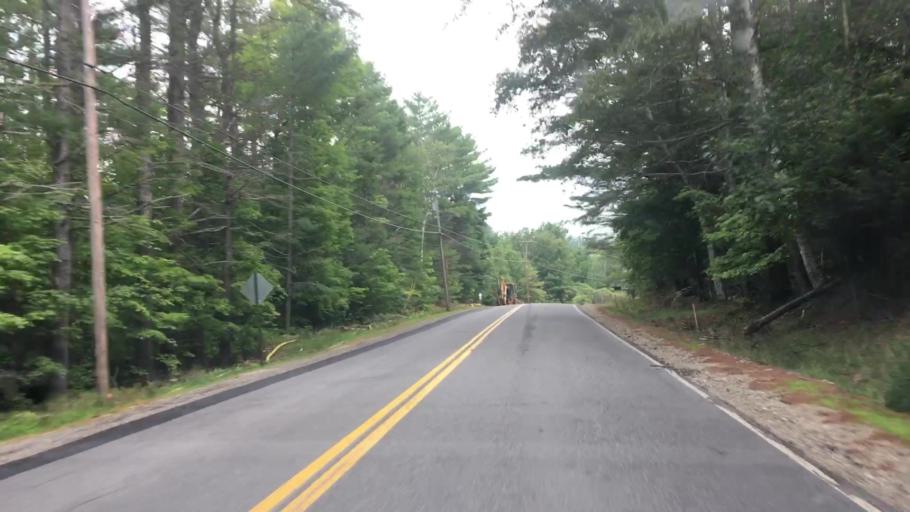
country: US
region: Maine
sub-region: Oxford County
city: Rumford
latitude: 44.5243
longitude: -70.6818
